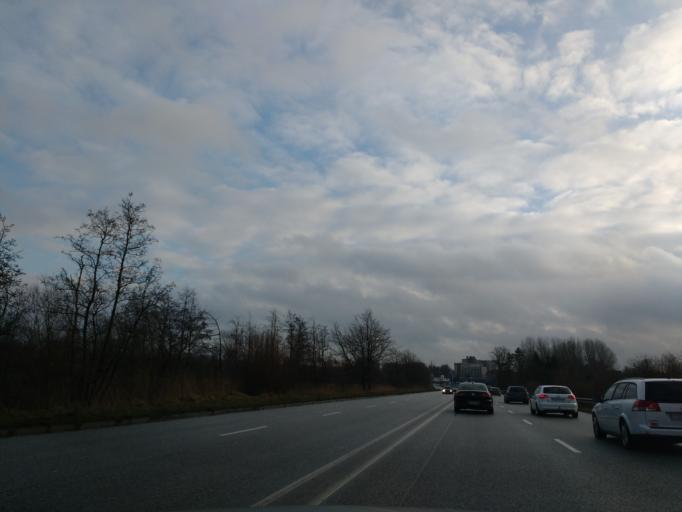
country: DE
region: Schleswig-Holstein
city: Eckernforde
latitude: 54.4678
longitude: 9.8314
